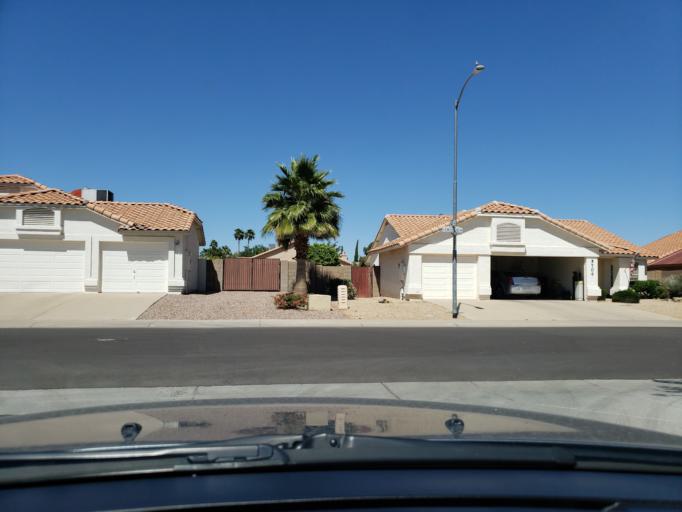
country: US
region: Arizona
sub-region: Maricopa County
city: Paradise Valley
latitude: 33.6164
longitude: -111.9596
